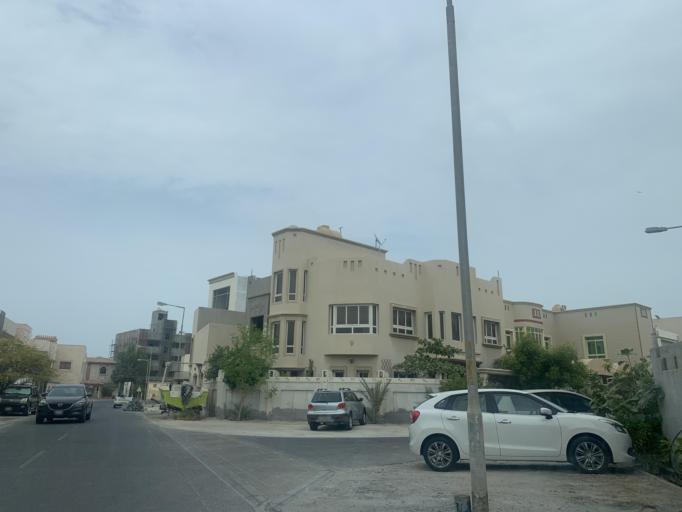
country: BH
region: Muharraq
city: Al Muharraq
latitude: 26.2806
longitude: 50.6382
